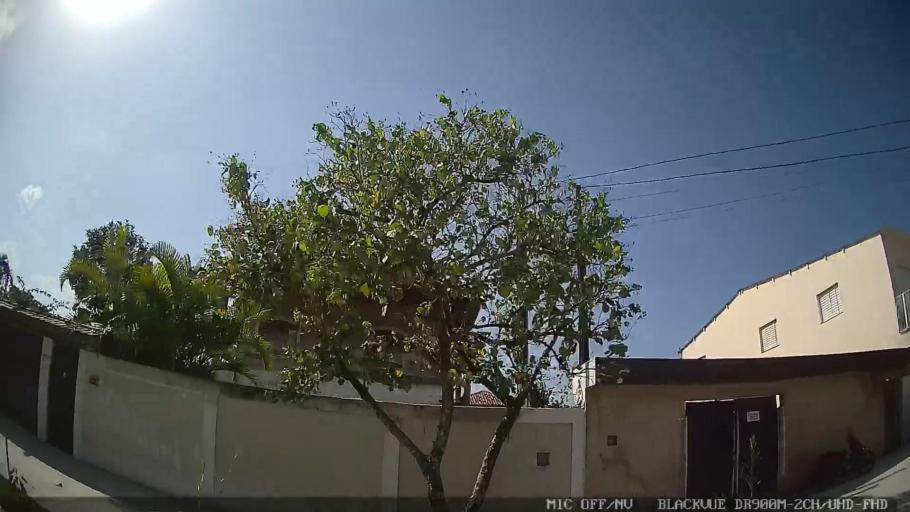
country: BR
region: Sao Paulo
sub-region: Guaruja
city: Guaruja
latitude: -23.9780
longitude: -46.1955
